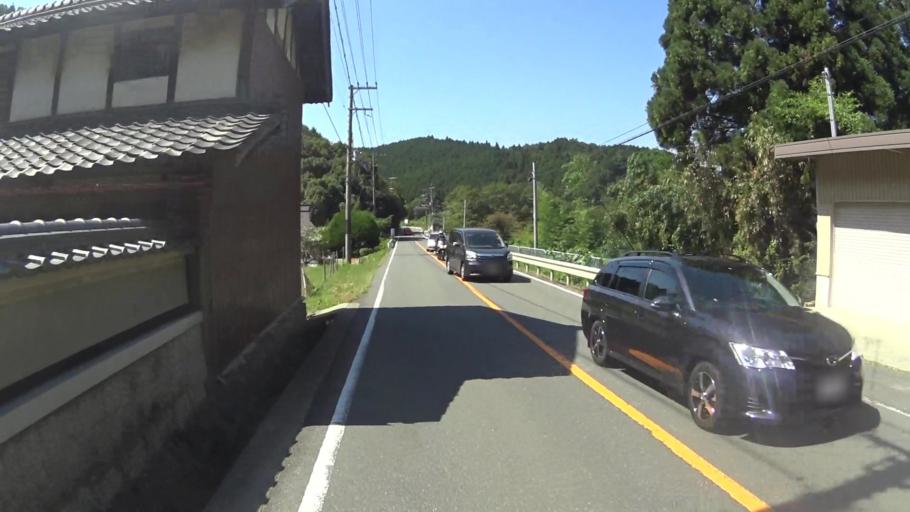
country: JP
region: Kyoto
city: Kameoka
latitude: 34.9527
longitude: 135.5066
